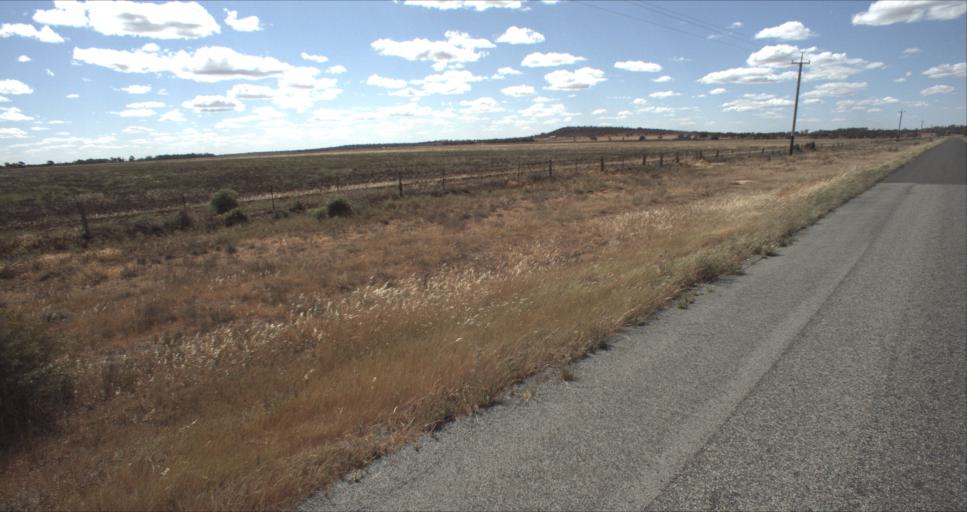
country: AU
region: New South Wales
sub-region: Leeton
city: Leeton
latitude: -34.4392
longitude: 146.2567
